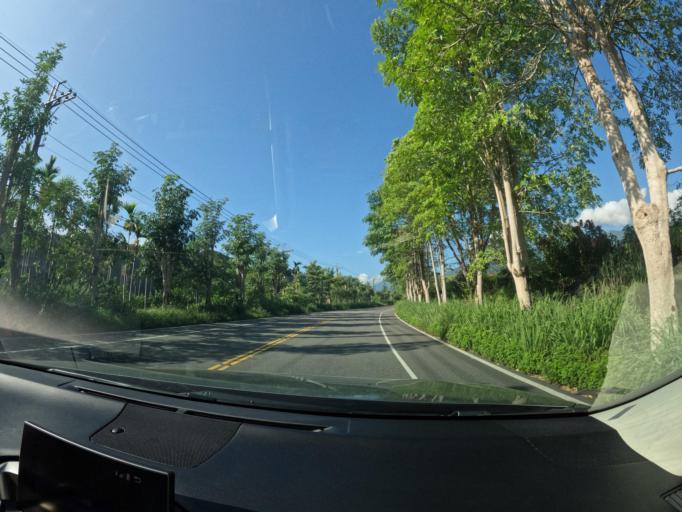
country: TW
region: Taiwan
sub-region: Hualien
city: Hualian
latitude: 23.4849
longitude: 121.3731
